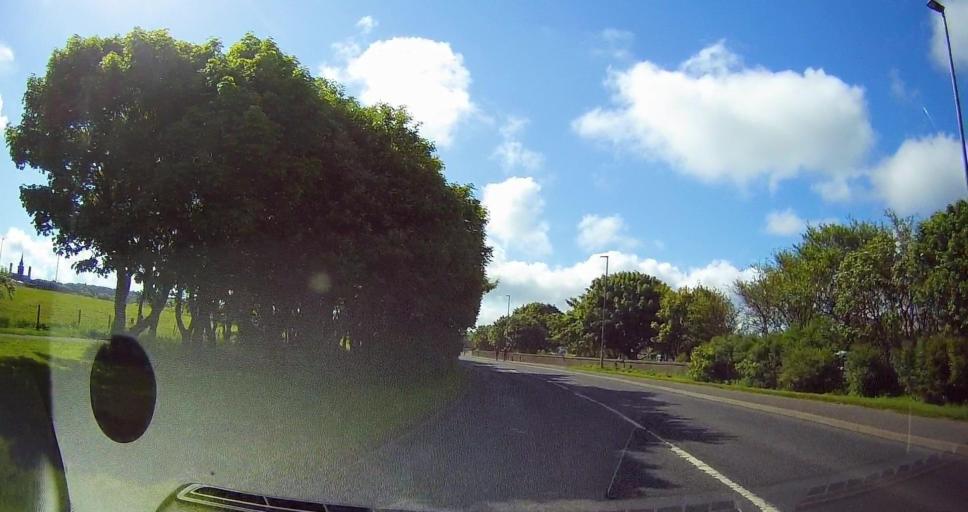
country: GB
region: Scotland
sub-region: Orkney Islands
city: Orkney
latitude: 58.9841
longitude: -2.9717
